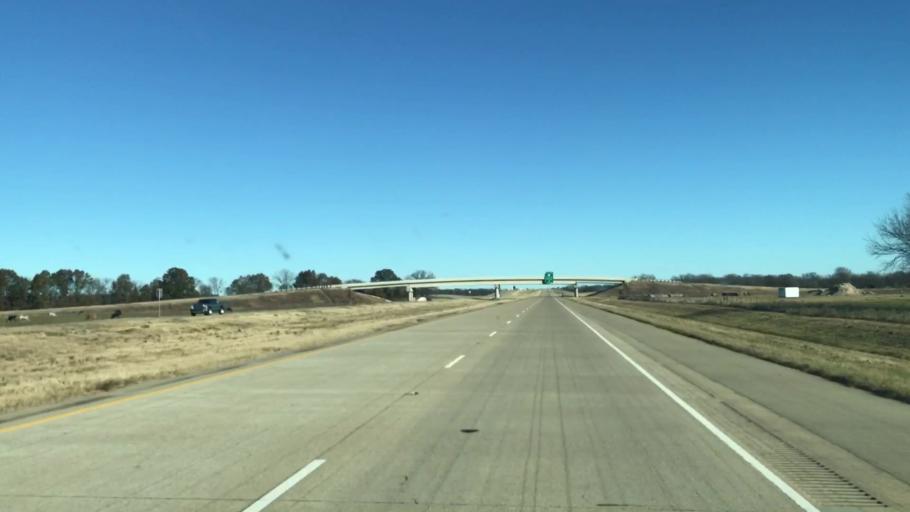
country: US
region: Louisiana
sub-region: Caddo Parish
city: Vivian
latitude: 32.8424
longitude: -93.8689
